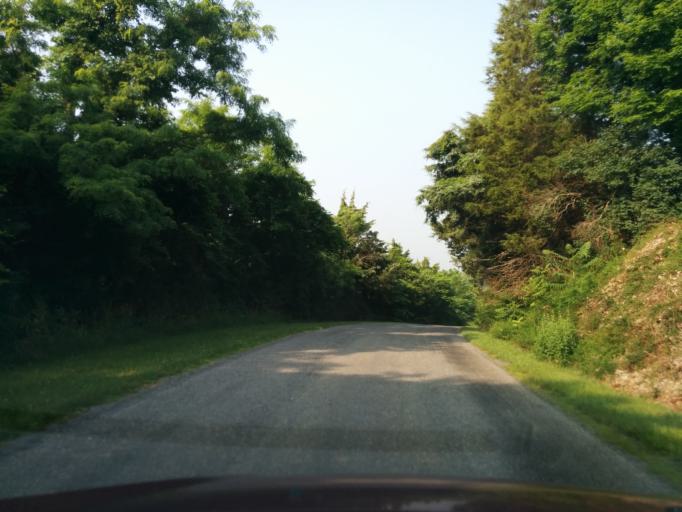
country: US
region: Virginia
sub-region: City of Lexington
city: Lexington
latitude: 37.7604
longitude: -79.4376
